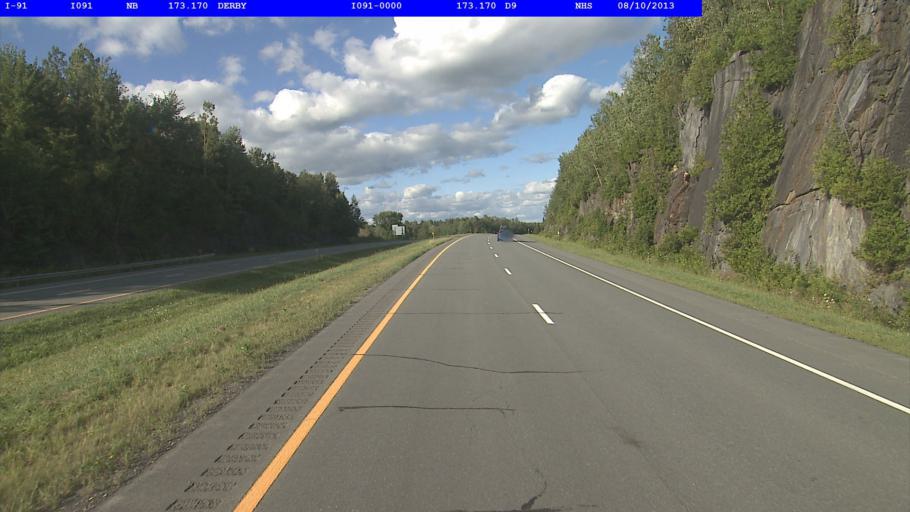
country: US
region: Vermont
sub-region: Orleans County
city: Newport
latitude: 44.9629
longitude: -72.1462
